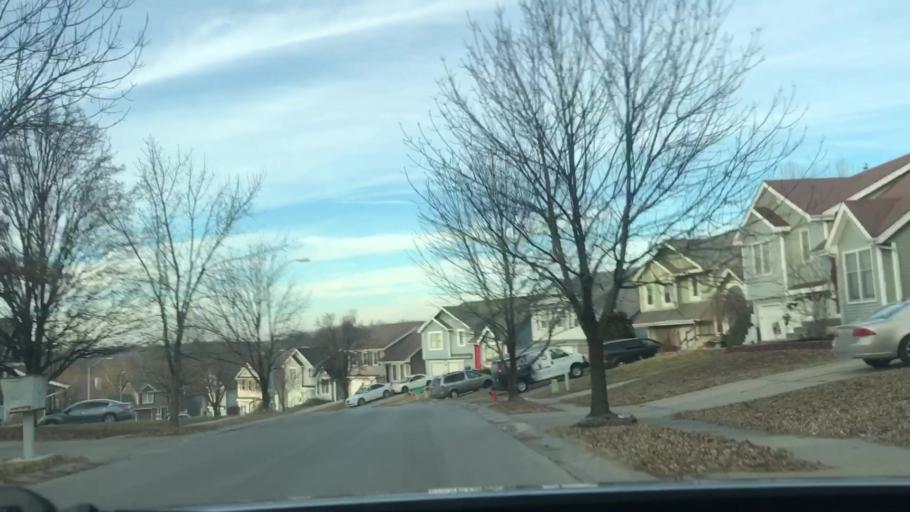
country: US
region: Missouri
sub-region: Platte County
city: Riverside
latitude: 39.2070
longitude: -94.5957
